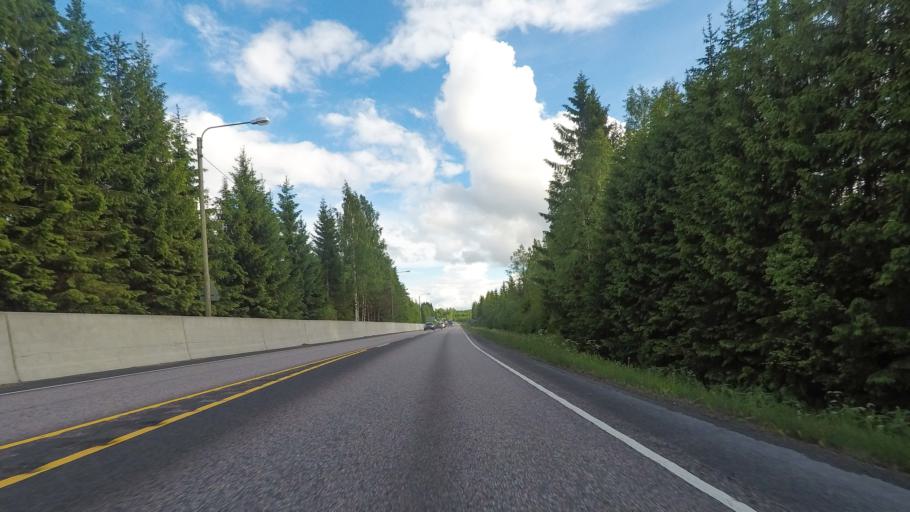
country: FI
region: Central Finland
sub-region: Joutsa
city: Joutsa
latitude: 61.7866
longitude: 26.0952
